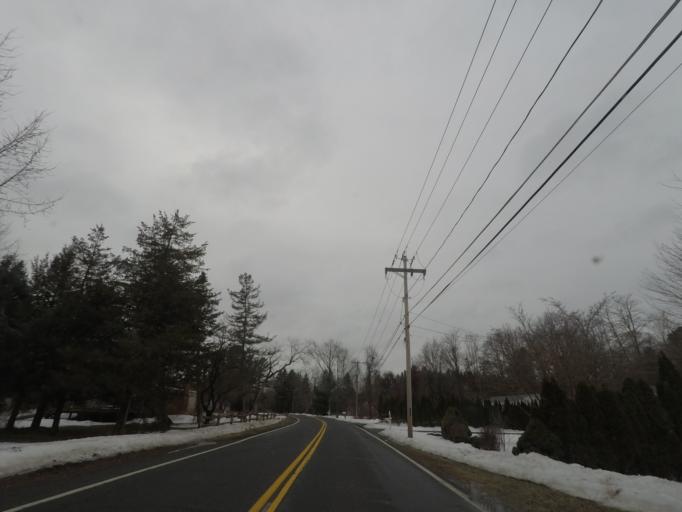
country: US
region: New York
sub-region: Schenectady County
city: Rotterdam
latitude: 42.7485
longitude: -73.9603
